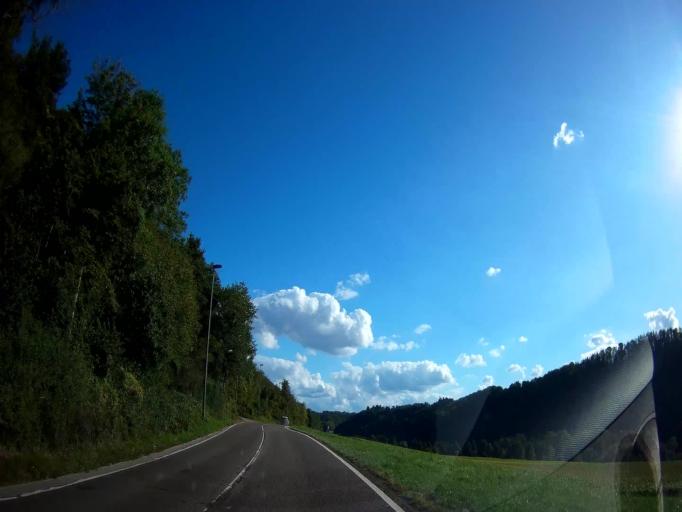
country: BE
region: Wallonia
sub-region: Province de Namur
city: Anhee
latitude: 50.2871
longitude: 4.8966
